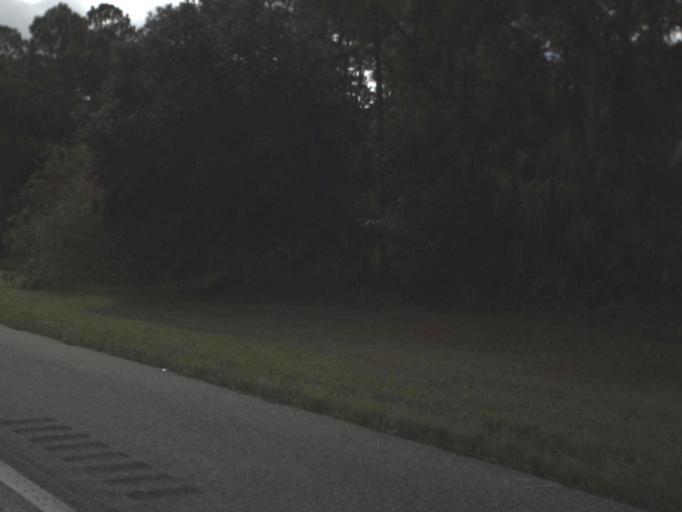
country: US
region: Florida
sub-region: Sarasota County
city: North Port
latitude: 27.0988
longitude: -82.1787
